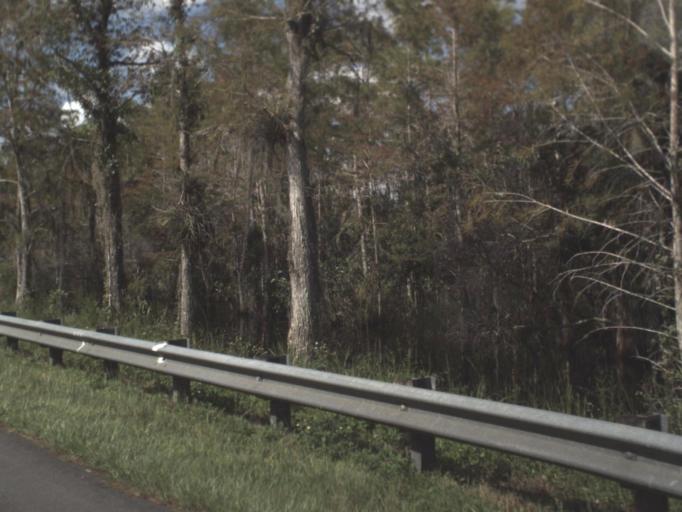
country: US
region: Florida
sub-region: Miami-Dade County
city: Kendall West
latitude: 25.8401
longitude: -80.9134
